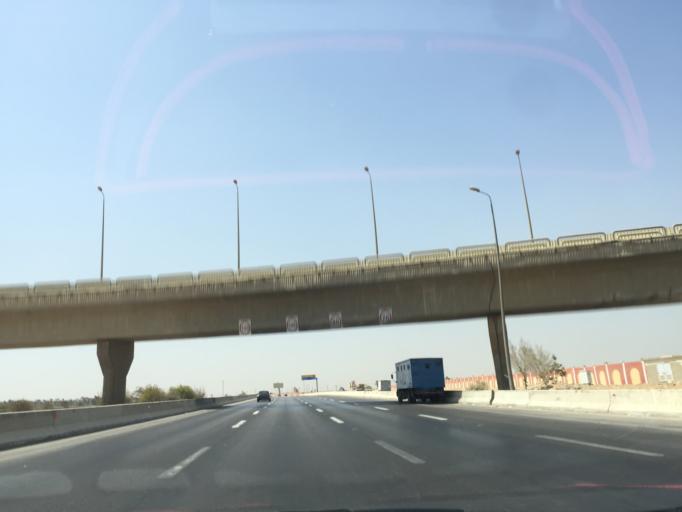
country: EG
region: Al Jizah
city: Awsim
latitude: 30.0808
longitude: 30.9957
